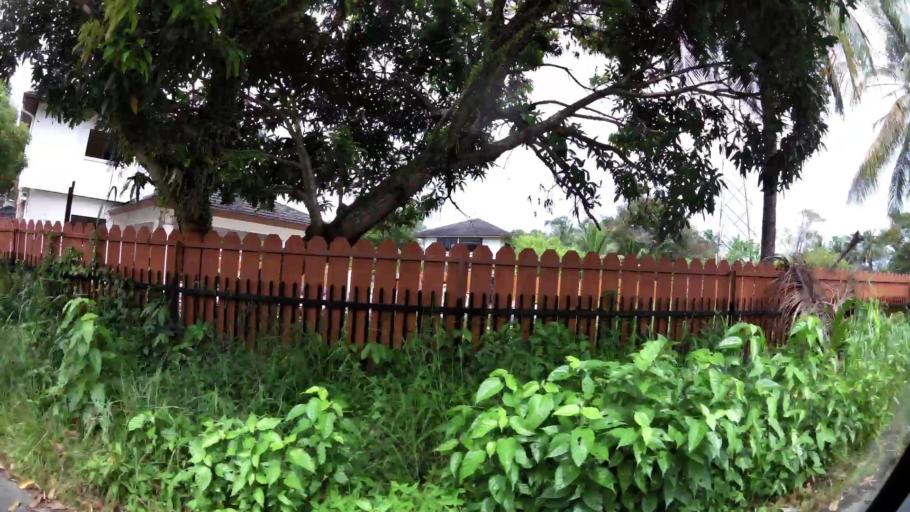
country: BN
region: Brunei and Muara
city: Bandar Seri Begawan
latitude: 4.9171
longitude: 114.9187
